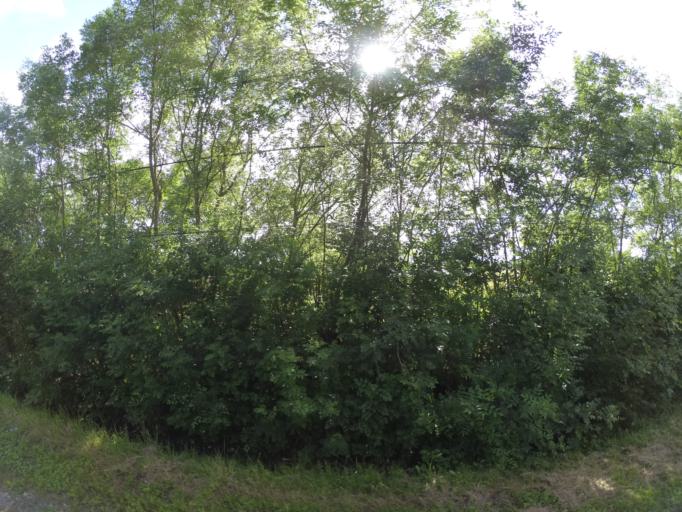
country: FR
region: Aquitaine
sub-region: Departement de la Gironde
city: Saint-Louis-de-Montferrand
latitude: 44.9585
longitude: -0.5510
